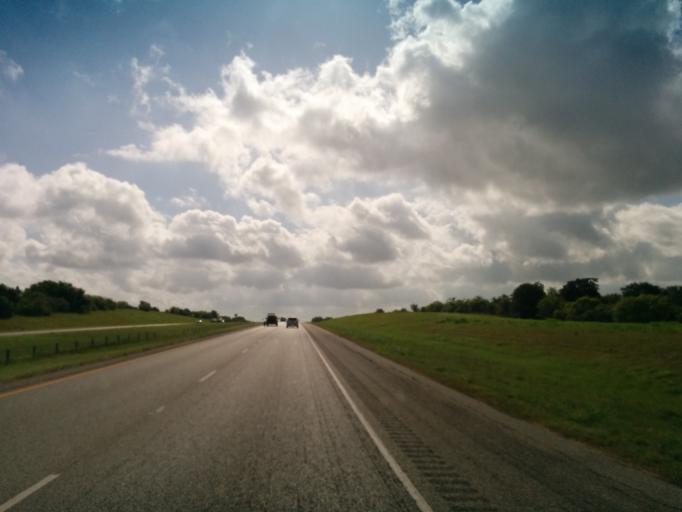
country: US
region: Texas
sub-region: Gonzales County
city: Waelder
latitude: 29.6641
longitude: -97.3629
